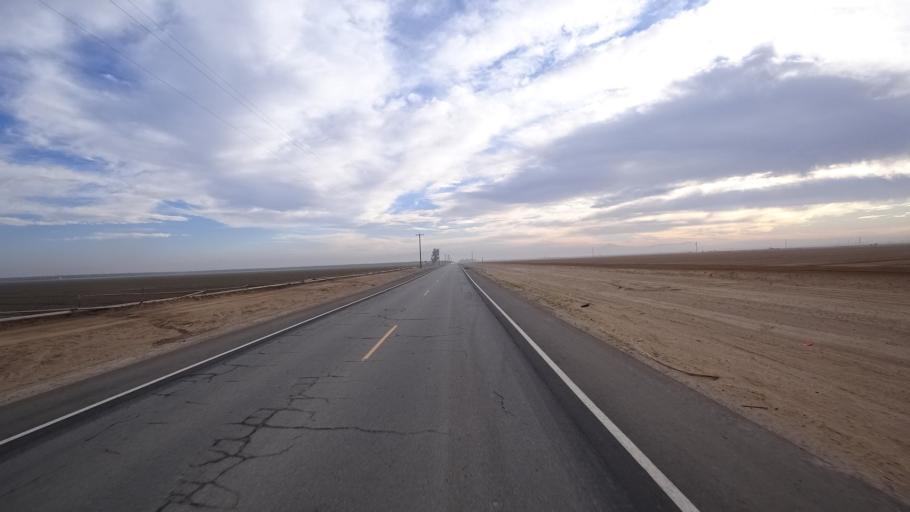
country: US
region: California
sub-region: Kern County
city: Rosedale
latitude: 35.4198
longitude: -119.2231
